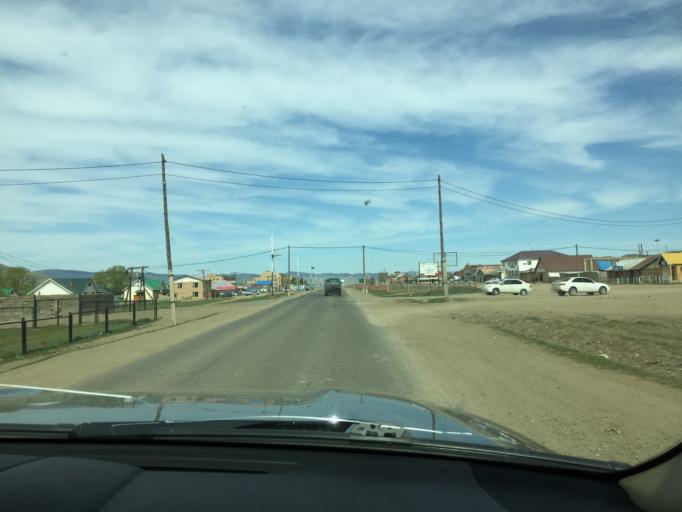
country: MN
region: Central Aimak
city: Ihsueuej
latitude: 48.2232
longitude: 106.2954
